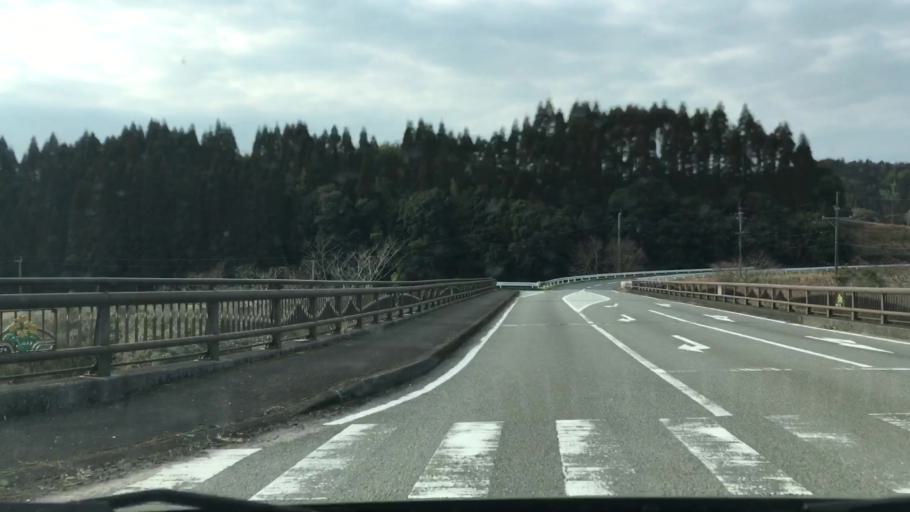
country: JP
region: Miyazaki
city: Nichinan
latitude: 31.6163
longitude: 131.3368
